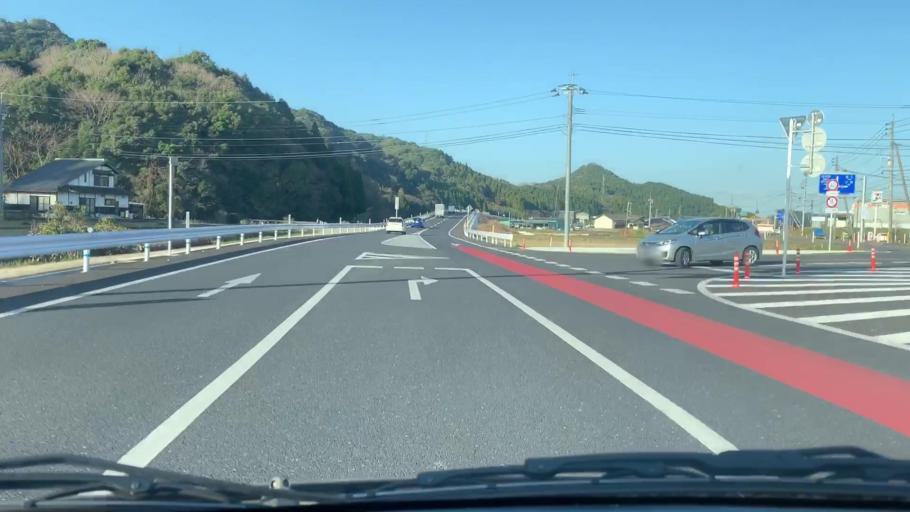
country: JP
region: Saga Prefecture
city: Takeocho-takeo
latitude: 33.2500
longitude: 129.9993
